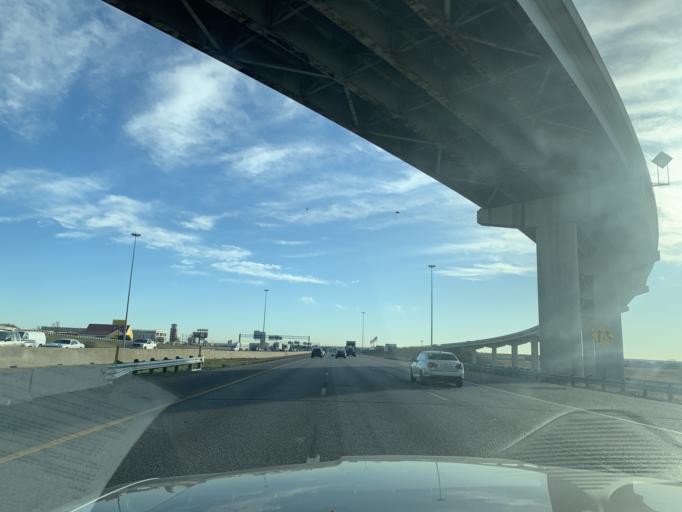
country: US
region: Texas
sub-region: Tarrant County
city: Arlington
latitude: 32.6772
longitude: -97.0625
